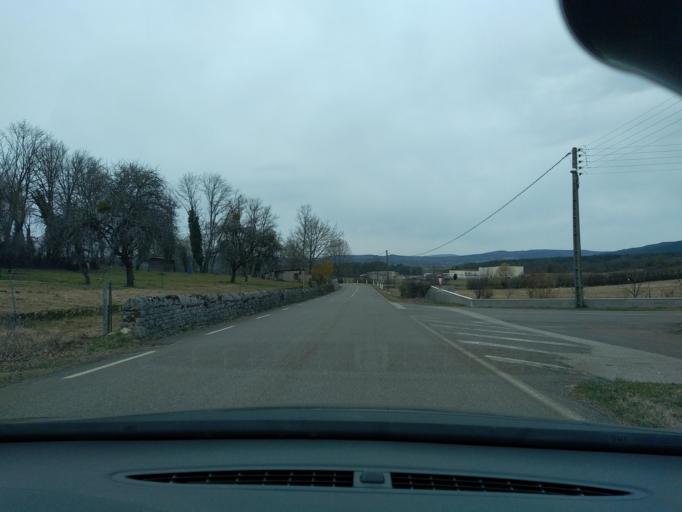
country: FR
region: Franche-Comte
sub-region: Departement du Jura
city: Arinthod
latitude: 46.3977
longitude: 5.5661
